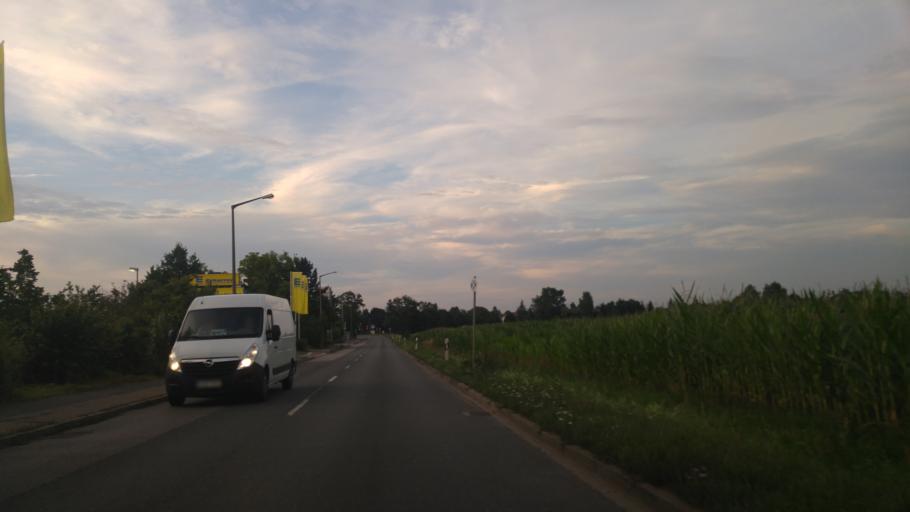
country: DE
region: Bavaria
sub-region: Regierungsbezirk Mittelfranken
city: Furth
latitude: 49.5201
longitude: 11.0064
